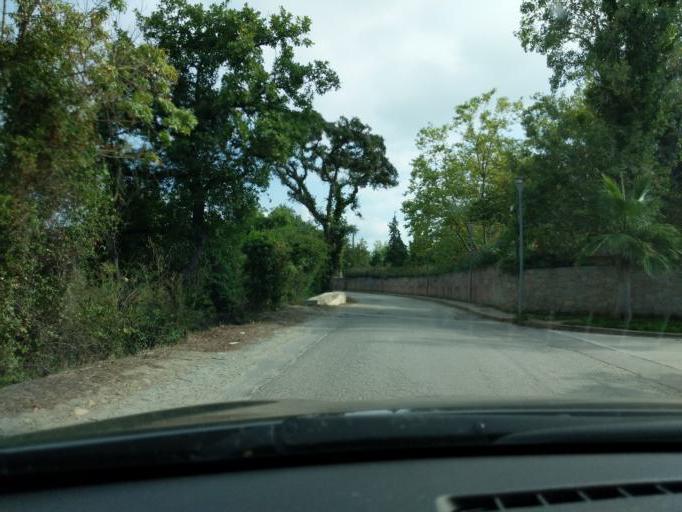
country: FR
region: Corsica
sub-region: Departement de la Haute-Corse
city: Ghisonaccia
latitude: 41.9996
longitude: 9.4432
